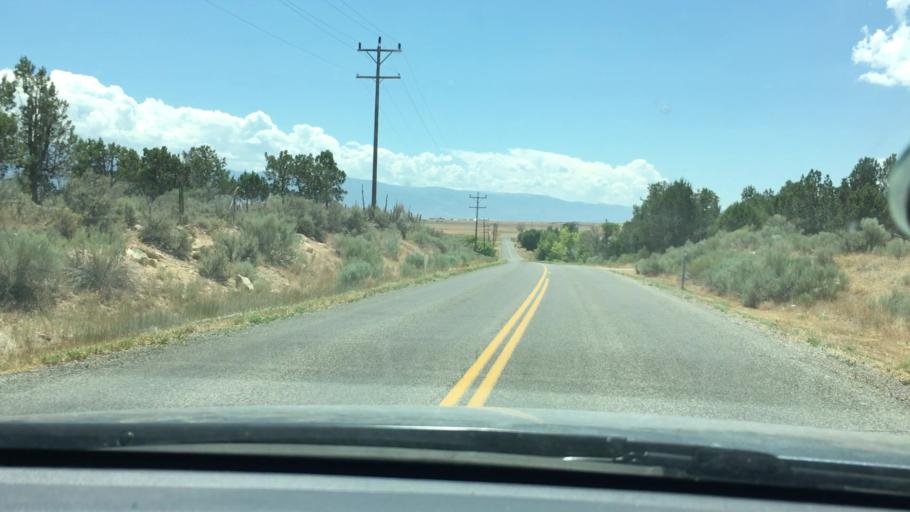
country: US
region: Utah
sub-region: Sanpete County
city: Fountain Green
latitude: 39.5902
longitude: -111.6424
